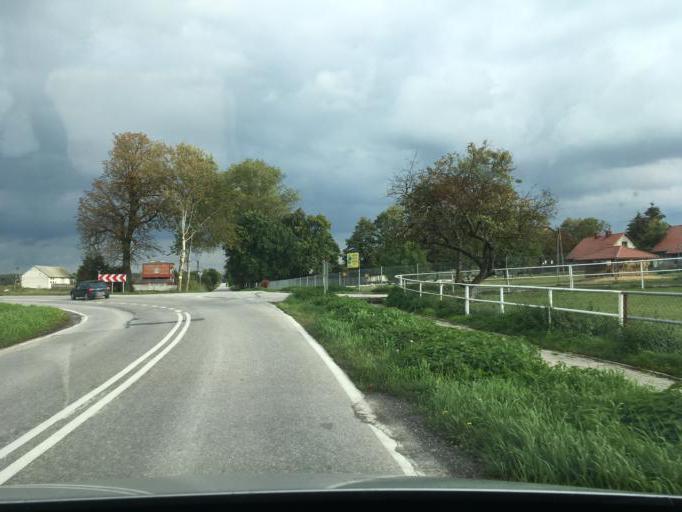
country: PL
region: Swietokrzyskie
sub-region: Powiat pinczowski
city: Michalow
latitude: 50.4948
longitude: 20.4643
